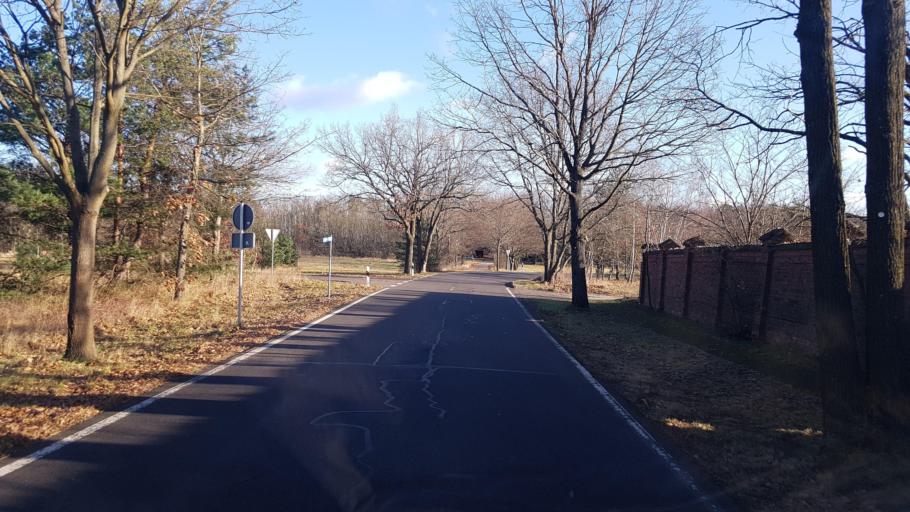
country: DE
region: Brandenburg
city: Heinersbruck
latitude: 51.7499
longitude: 14.5462
